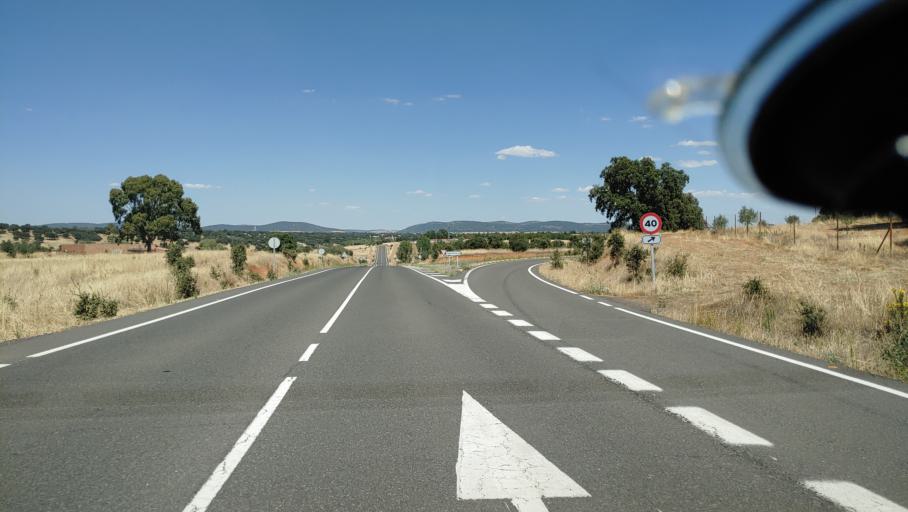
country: ES
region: Castille-La Mancha
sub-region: Provincia de Ciudad Real
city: Saceruela
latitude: 38.9409
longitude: -4.6164
